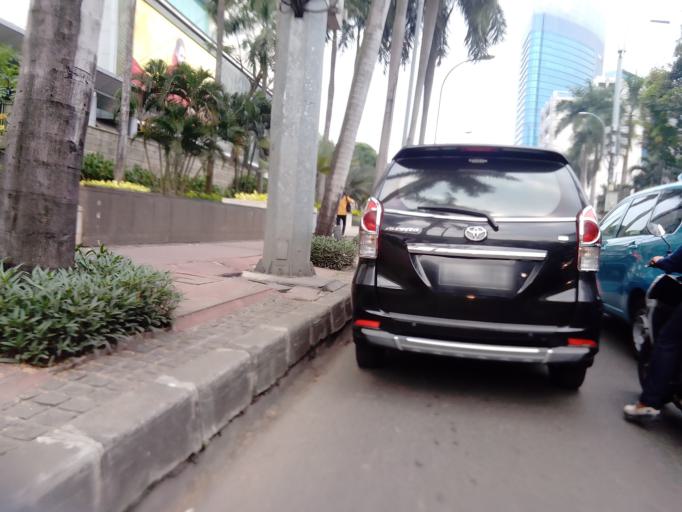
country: ID
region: Jakarta Raya
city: Jakarta
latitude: -6.1964
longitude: 106.8219
